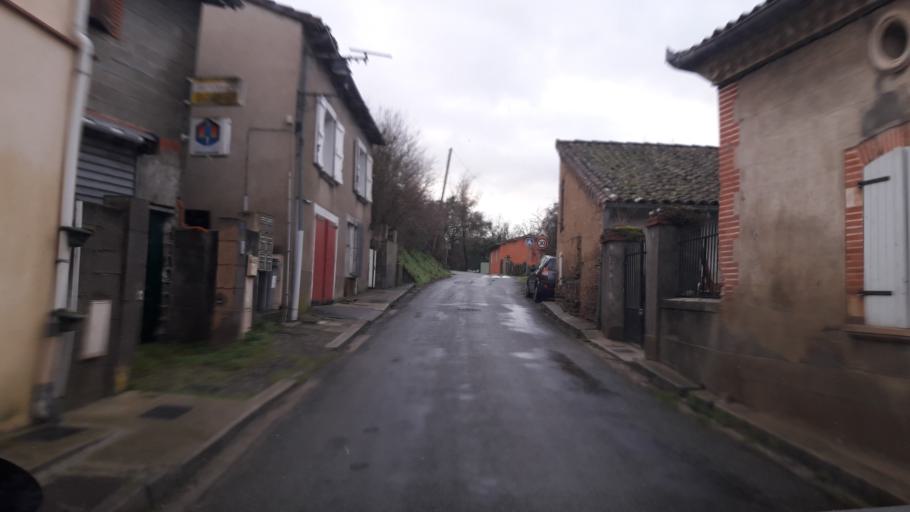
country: FR
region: Midi-Pyrenees
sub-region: Departement de la Haute-Garonne
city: Marquefave
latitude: 43.3167
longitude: 1.2456
